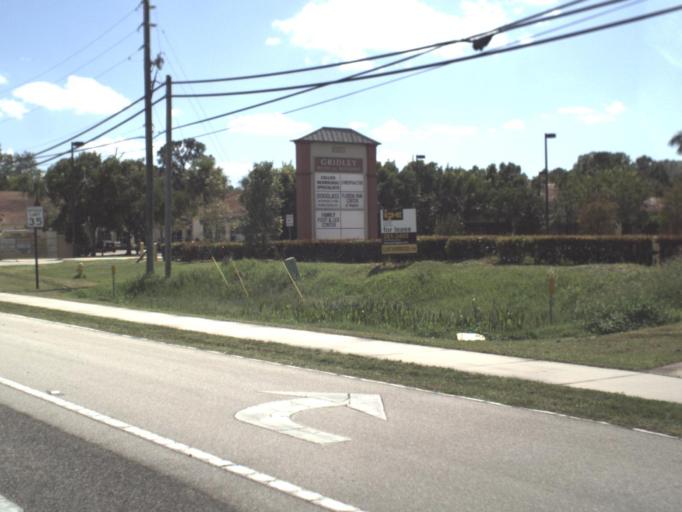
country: US
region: Florida
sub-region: Collier County
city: Lely Resort
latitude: 26.0689
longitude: -81.7081
